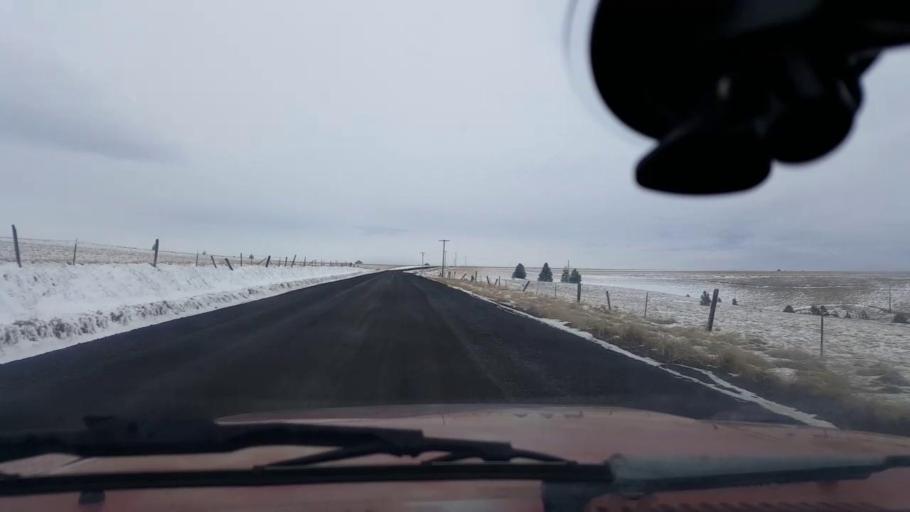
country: US
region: Washington
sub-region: Garfield County
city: Pomeroy
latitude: 46.3196
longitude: -117.4016
